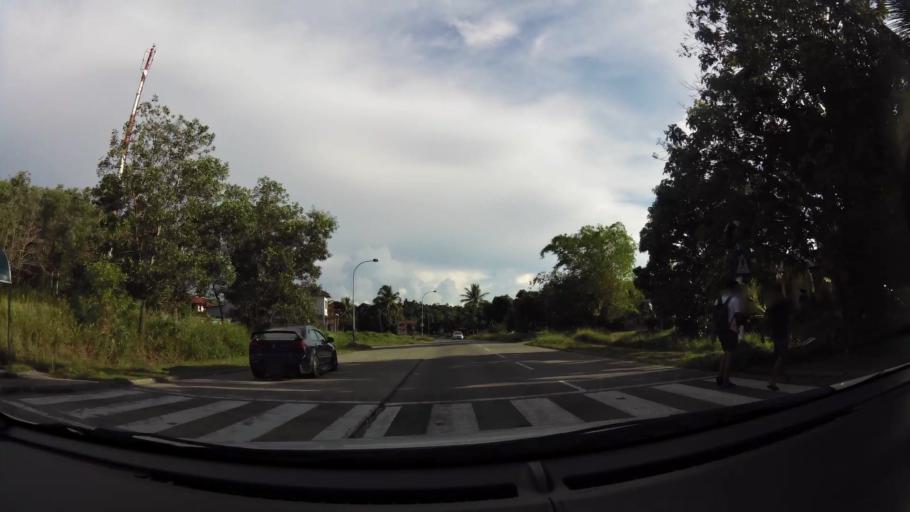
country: BN
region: Brunei and Muara
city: Bandar Seri Begawan
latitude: 4.9822
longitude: 114.9686
